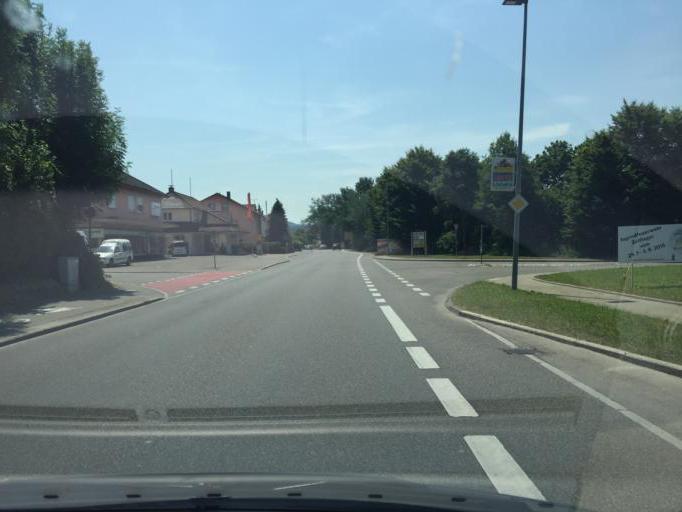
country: DE
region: Baden-Wuerttemberg
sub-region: Freiburg Region
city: Rielasingen-Worblingen
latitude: 47.7377
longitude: 8.8406
